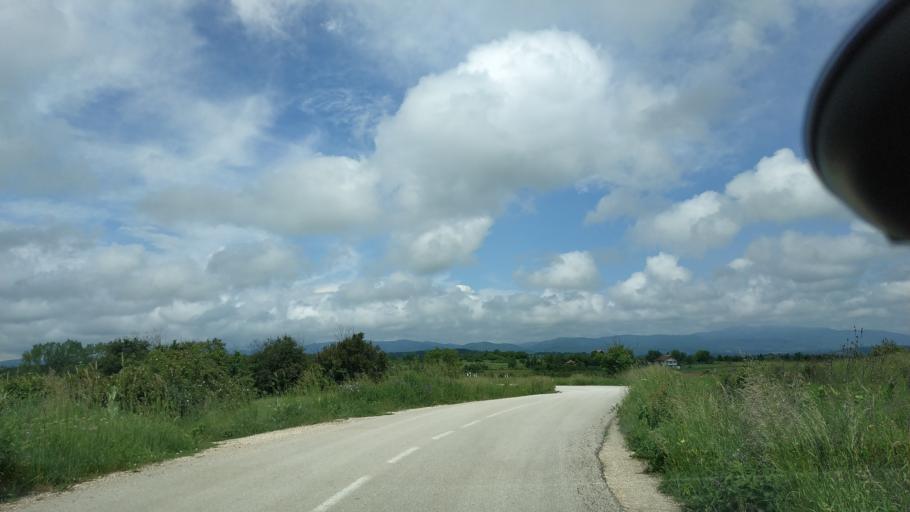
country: RS
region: Central Serbia
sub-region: Zajecarski Okrug
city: Boljevac
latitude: 43.8145
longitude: 21.9524
